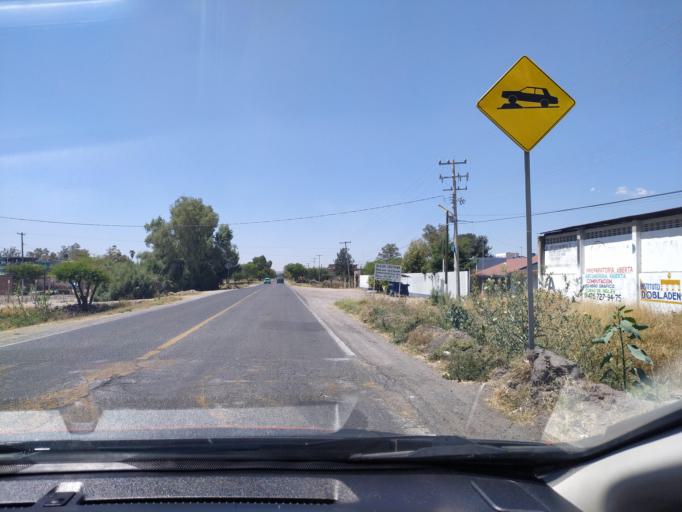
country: MX
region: Guanajuato
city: Ciudad Manuel Doblado
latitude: 20.7412
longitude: -101.8848
